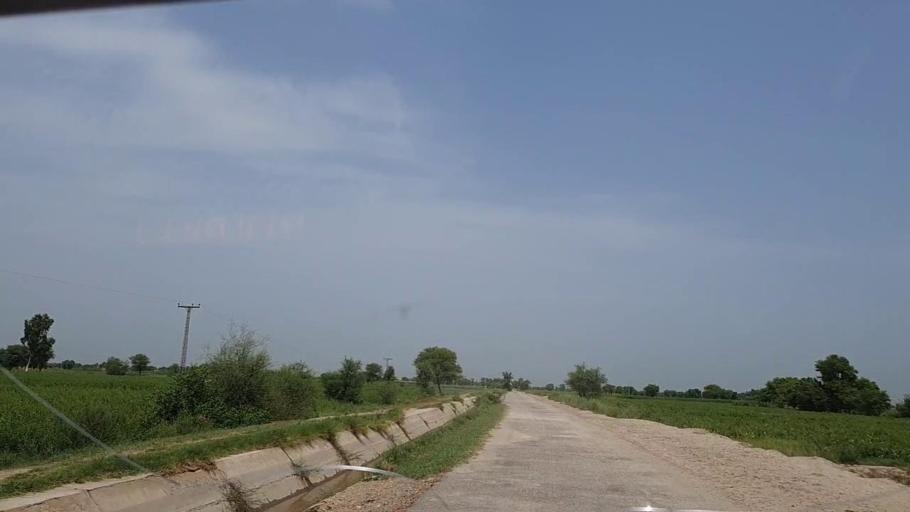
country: PK
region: Sindh
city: Tharu Shah
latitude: 26.9294
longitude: 68.0684
